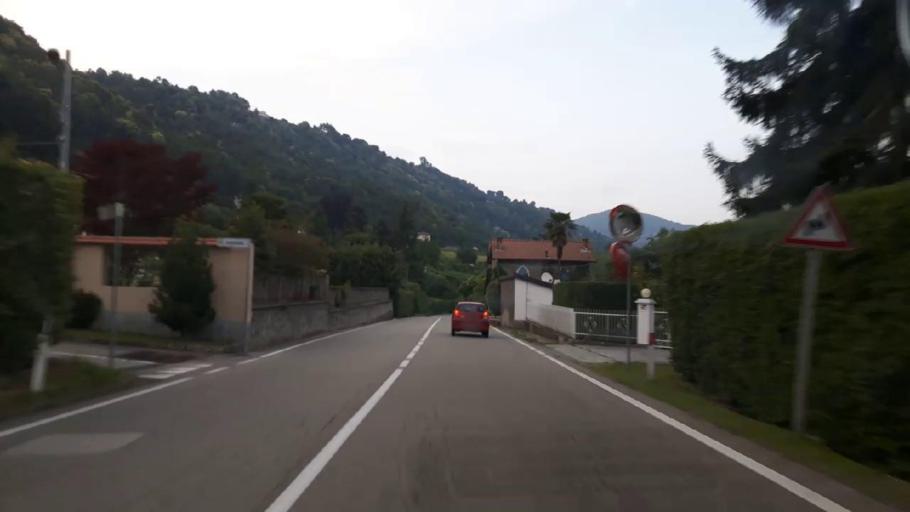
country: IT
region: Piedmont
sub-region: Provincia di Novara
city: Meina
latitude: 45.8042
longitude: 8.5406
